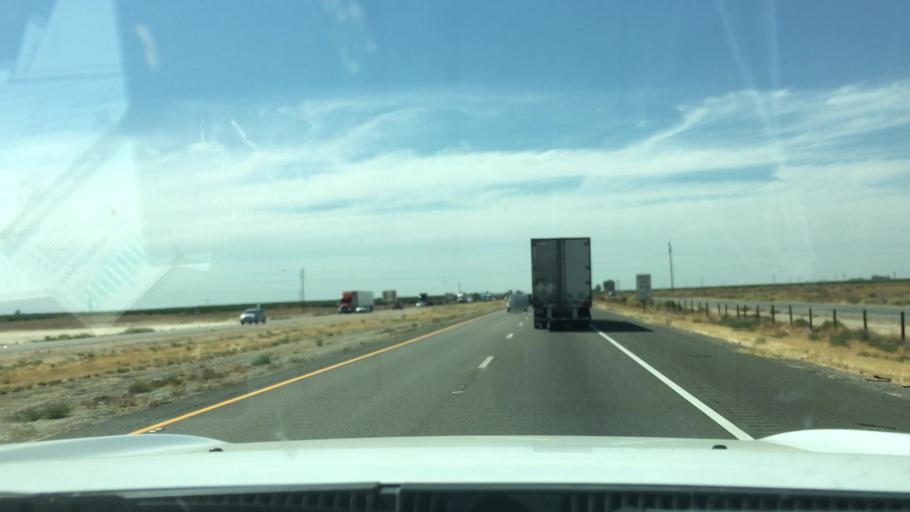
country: US
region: California
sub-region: Kern County
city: Buttonwillow
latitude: 35.4060
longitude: -119.4068
